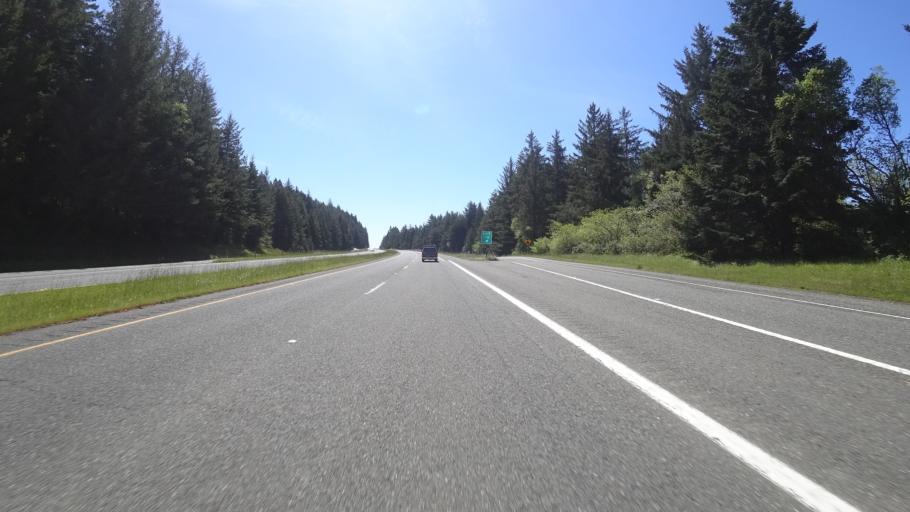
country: US
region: California
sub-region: Humboldt County
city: Westhaven-Moonstone
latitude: 41.1007
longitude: -124.1542
